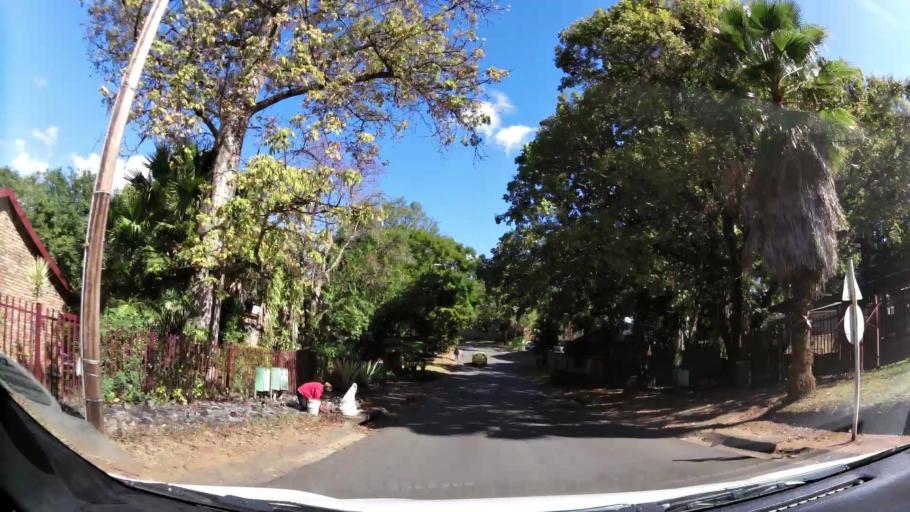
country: ZA
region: Limpopo
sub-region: Mopani District Municipality
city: Tzaneen
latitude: -23.8257
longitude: 30.1475
